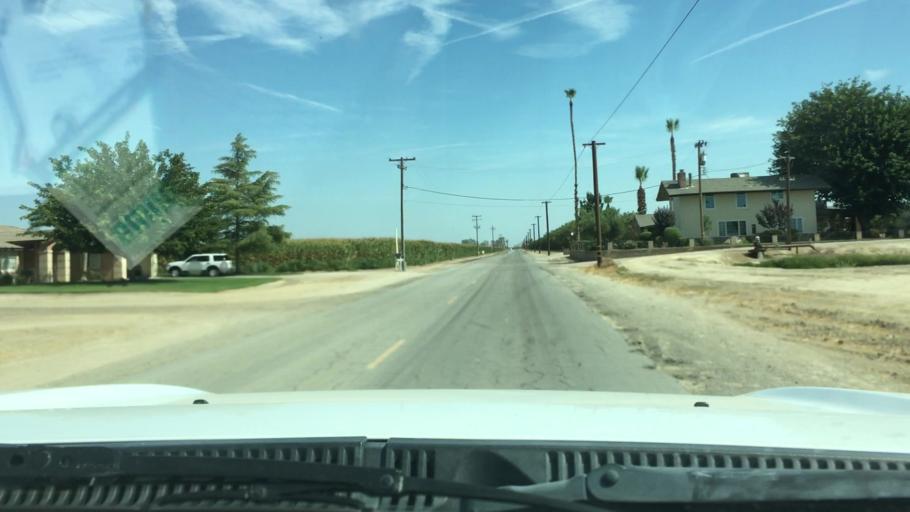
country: US
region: California
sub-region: Kern County
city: Buttonwillow
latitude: 35.4197
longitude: -119.3764
